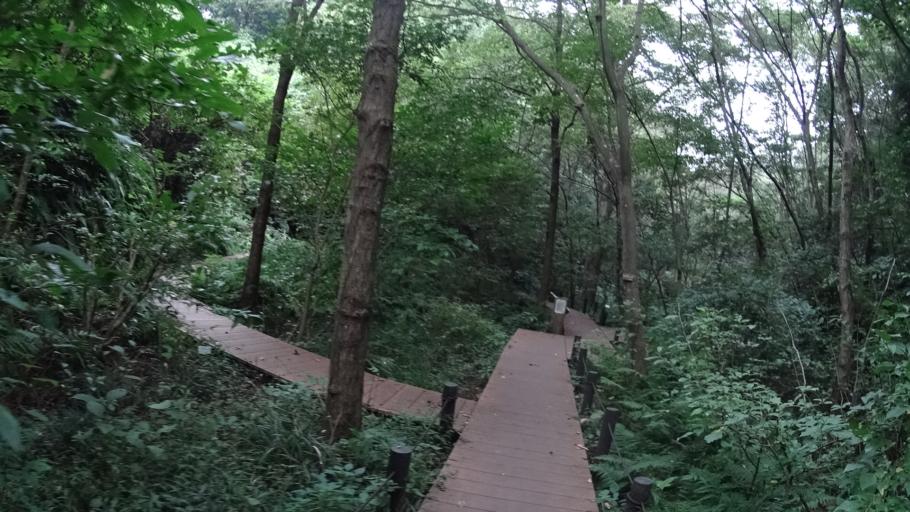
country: JP
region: Kanagawa
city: Zushi
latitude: 35.3518
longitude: 139.5992
